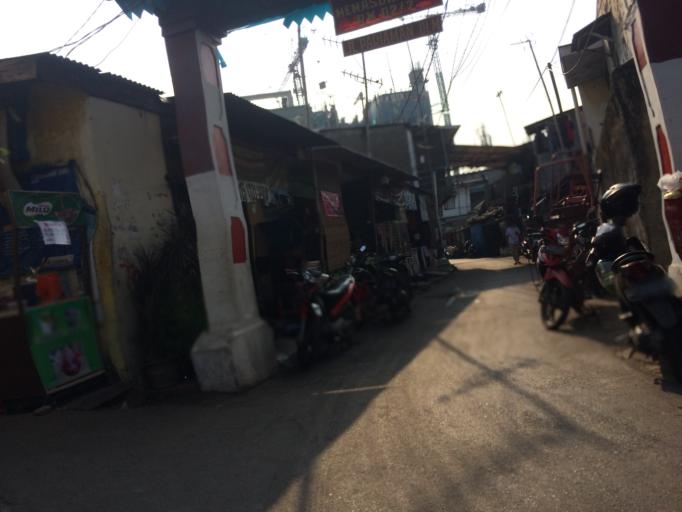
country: ID
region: Jakarta Raya
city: Jakarta
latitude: -6.2087
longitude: 106.8431
